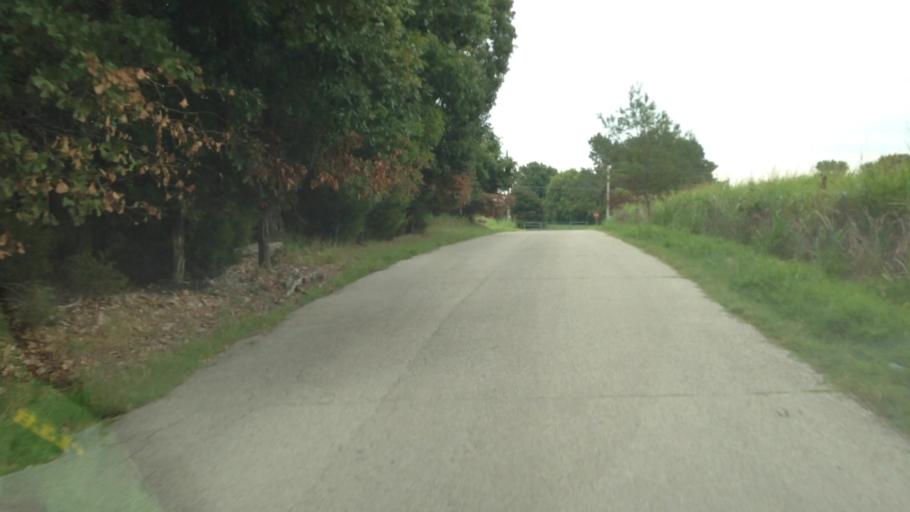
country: US
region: Oklahoma
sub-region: Delaware County
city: Cleora
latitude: 36.5465
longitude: -94.9632
